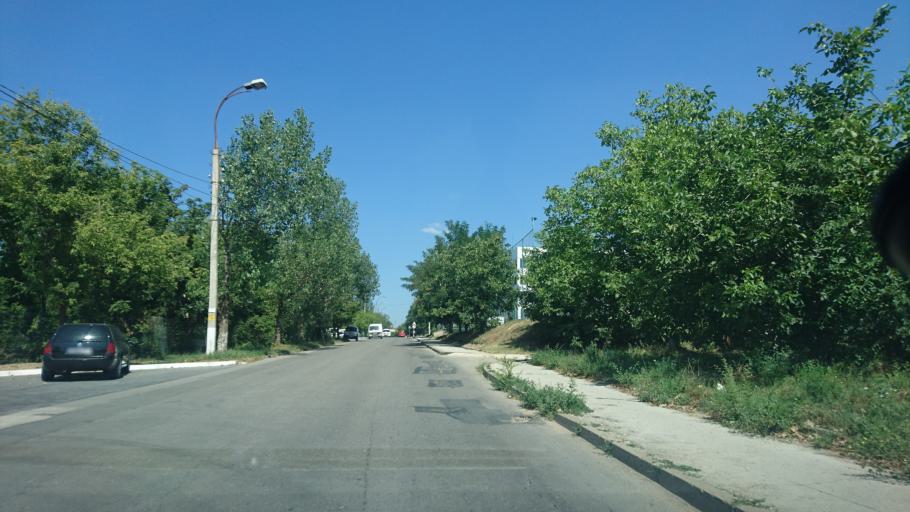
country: MD
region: Laloveni
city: Ialoveni
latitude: 46.9944
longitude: 28.7866
